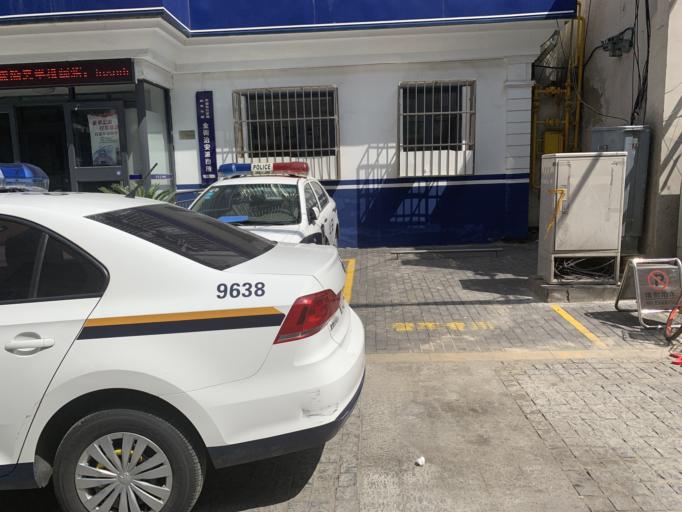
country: CN
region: Tianjin Shi
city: Quanyechang
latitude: 39.1241
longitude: 117.1953
